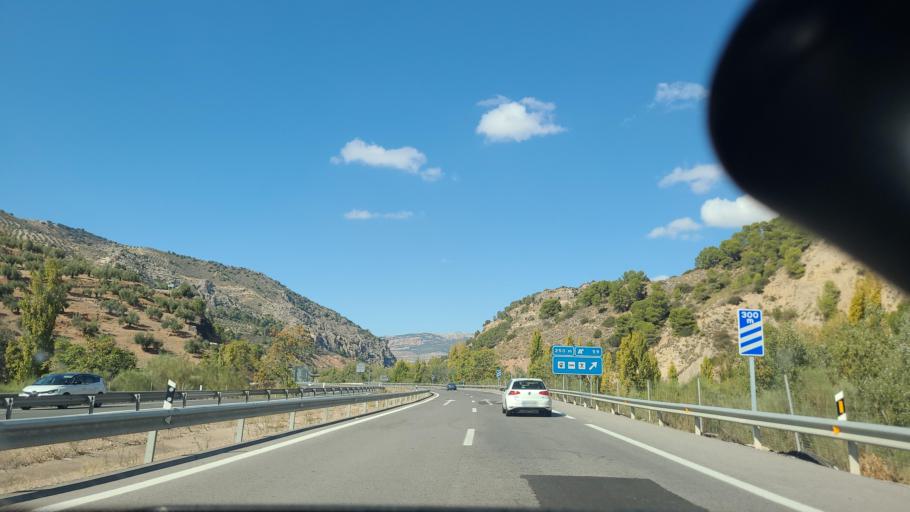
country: ES
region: Andalusia
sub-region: Provincia de Jaen
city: Cambil
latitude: 37.6697
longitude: -3.6199
